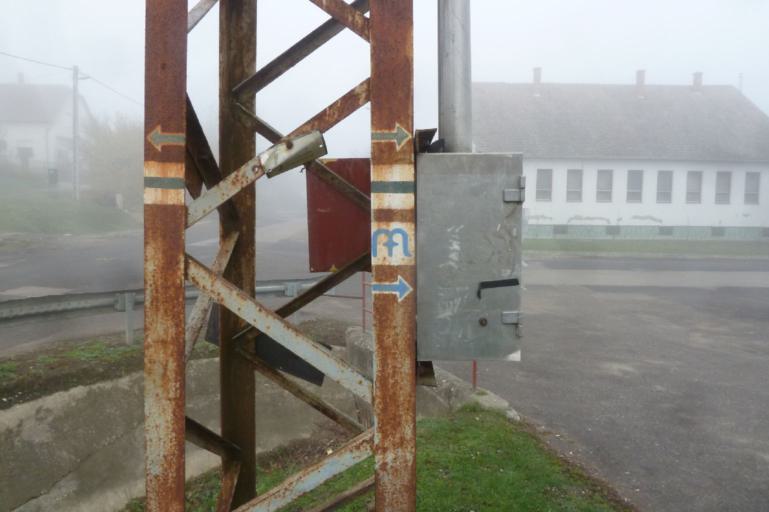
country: HU
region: Pest
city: Galgamacsa
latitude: 47.6919
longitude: 19.3879
